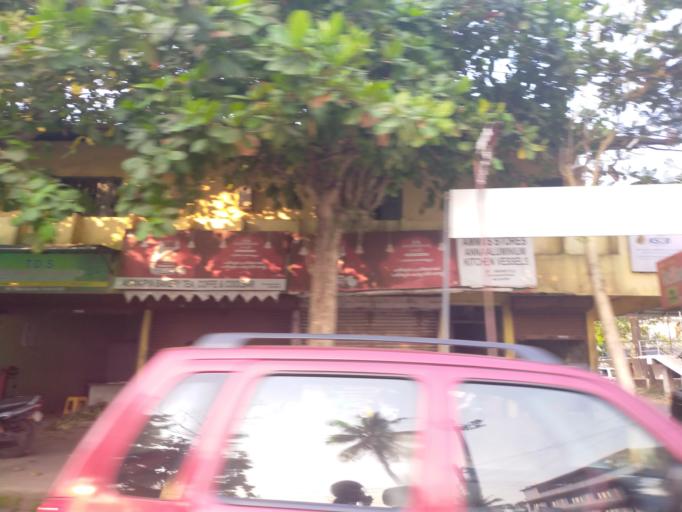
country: IN
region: Kerala
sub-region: Kottayam
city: Palackattumala
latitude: 9.7416
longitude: 76.5150
